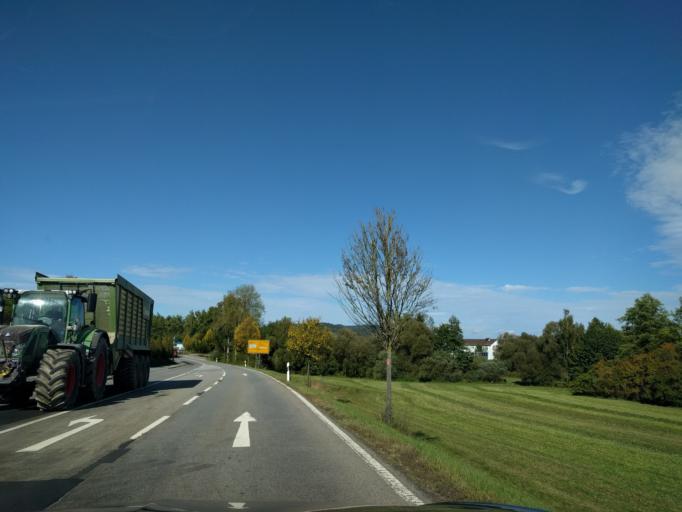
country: DE
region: Bavaria
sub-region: Upper Palatinate
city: Kotzting
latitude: 49.1697
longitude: 12.8674
